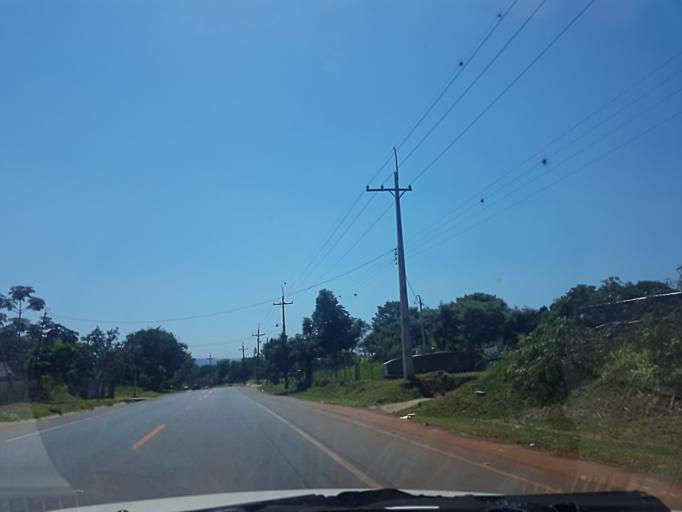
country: PY
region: Central
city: Aregua
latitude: -25.2394
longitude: -57.4291
